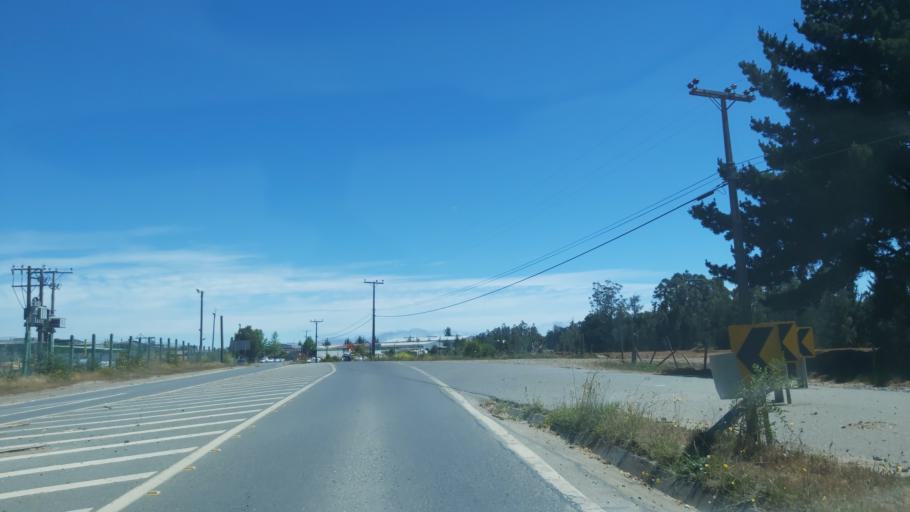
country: CL
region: Maule
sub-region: Provincia de Talca
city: Constitucion
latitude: -35.3712
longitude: -72.4129
